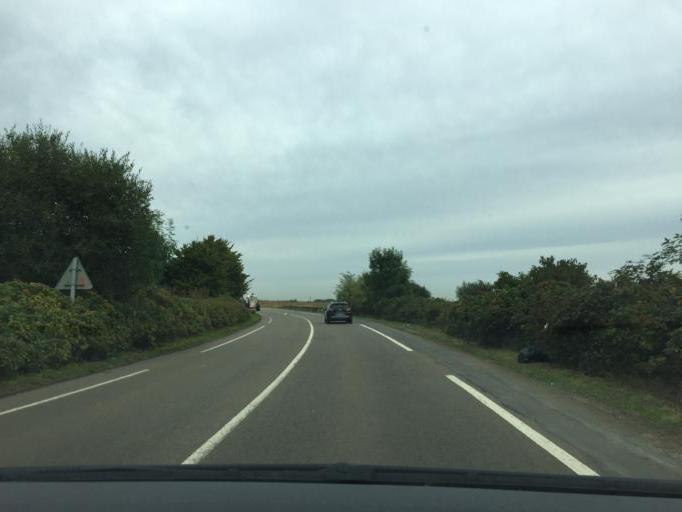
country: FR
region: Ile-de-France
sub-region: Departement de l'Essonne
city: Villiers-le-Bacle
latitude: 48.7432
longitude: 2.1209
